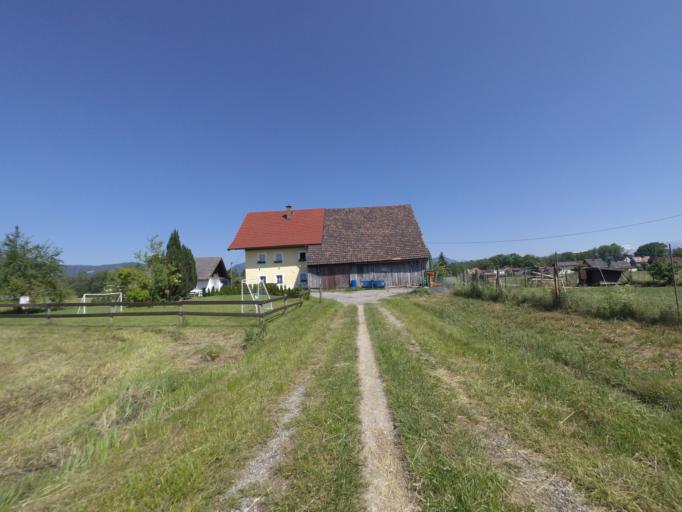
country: AT
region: Salzburg
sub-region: Politischer Bezirk Salzburg-Umgebung
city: Grodig
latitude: 47.7621
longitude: 13.0302
